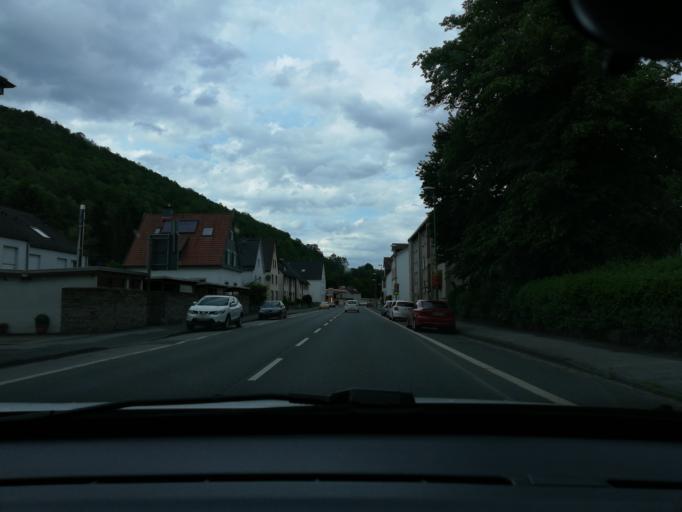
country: DE
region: North Rhine-Westphalia
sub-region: Regierungsbezirk Arnsberg
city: Schalksmuhle
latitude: 51.2891
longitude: 7.5207
